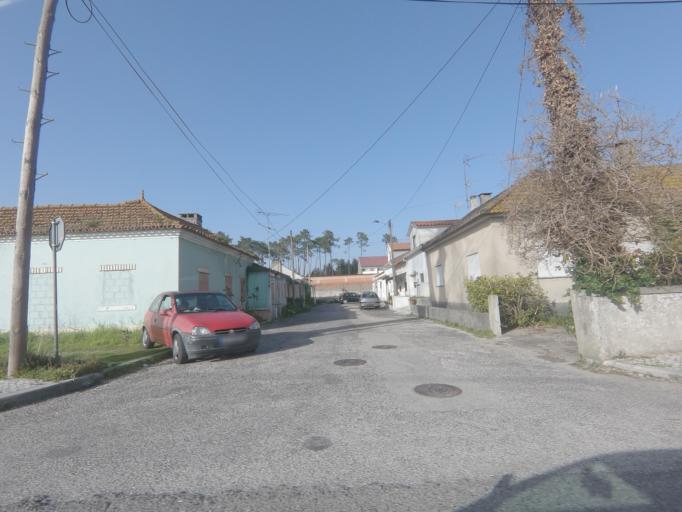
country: PT
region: Leiria
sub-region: Marinha Grande
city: Marinha Grande
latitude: 39.7485
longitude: -8.9151
